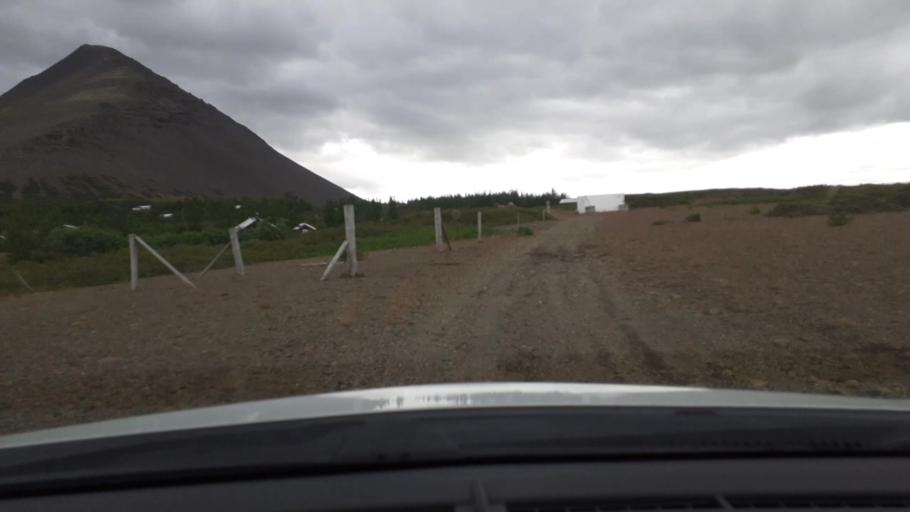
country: IS
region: West
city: Borgarnes
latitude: 64.4598
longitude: -21.9559
